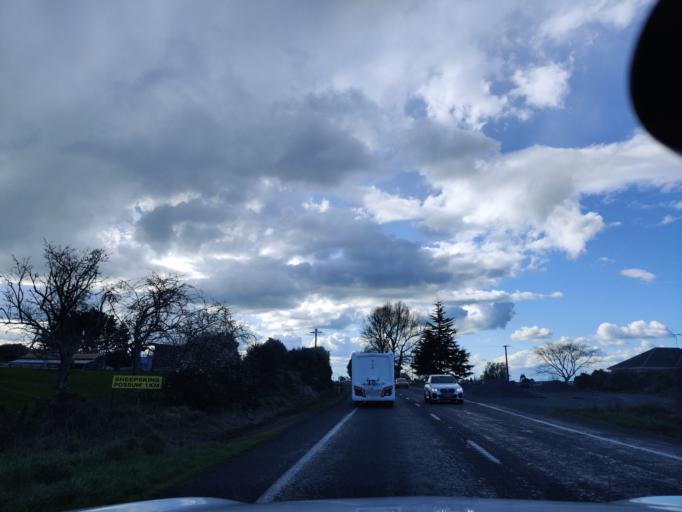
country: NZ
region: Waikato
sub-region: South Waikato District
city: Tokoroa
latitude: -38.1166
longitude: 175.8238
